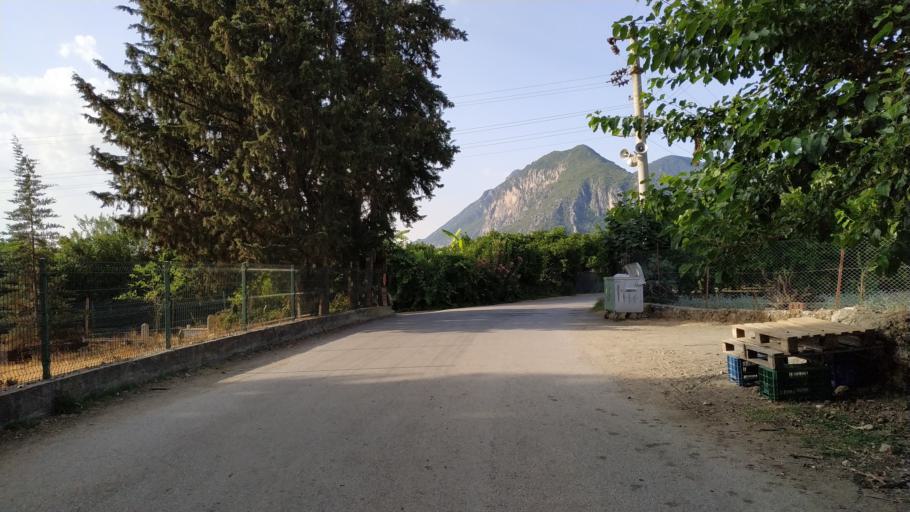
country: TR
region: Antalya
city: Tekirova
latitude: 36.4094
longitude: 30.4754
